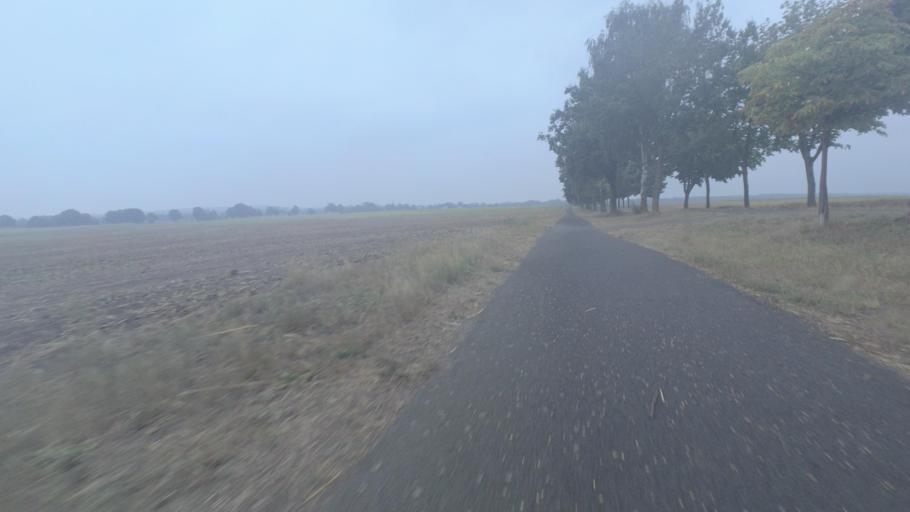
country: DE
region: Brandenburg
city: Heiligengrabe
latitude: 53.1287
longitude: 12.3753
